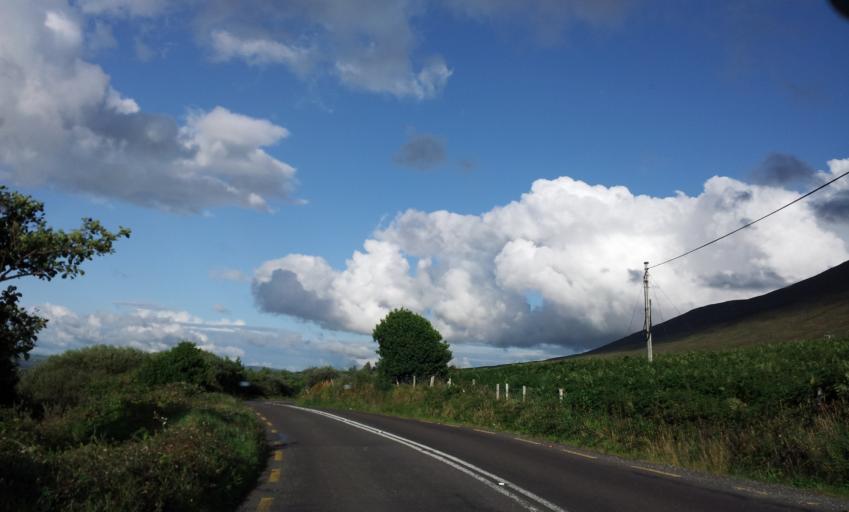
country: IE
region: Munster
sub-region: Ciarrai
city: Killorglin
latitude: 52.2313
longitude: -9.8688
